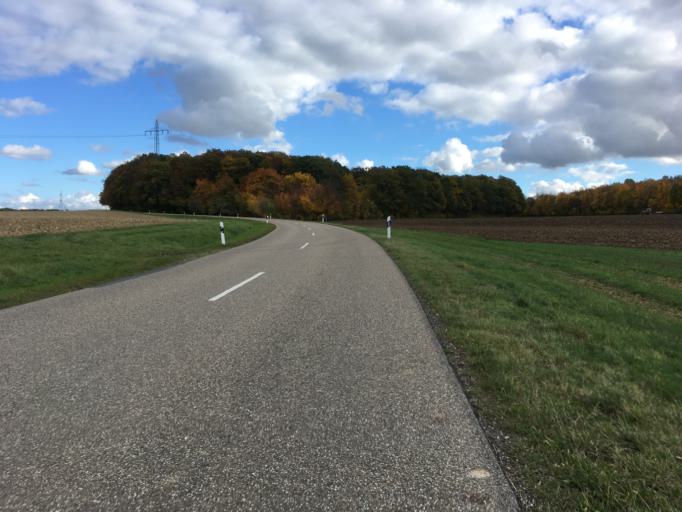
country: DE
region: Baden-Wuerttemberg
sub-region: Regierungsbezirk Stuttgart
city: Untermunkheim
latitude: 49.1871
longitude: 9.7379
